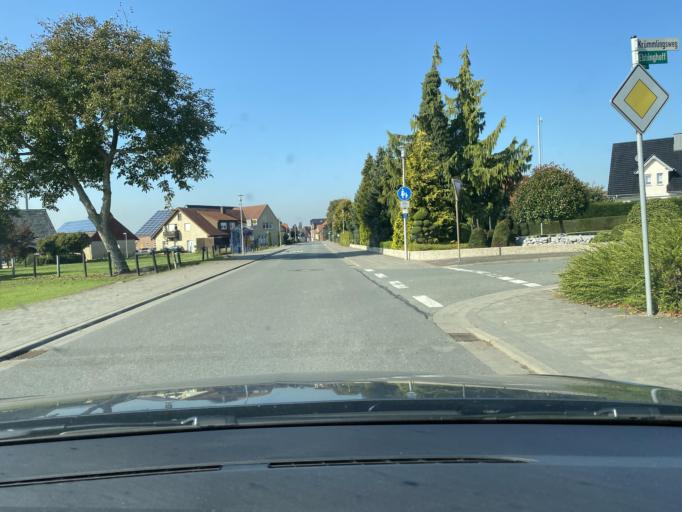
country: DE
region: North Rhine-Westphalia
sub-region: Regierungsbezirk Munster
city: Schoppingen
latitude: 52.0894
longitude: 7.2438
